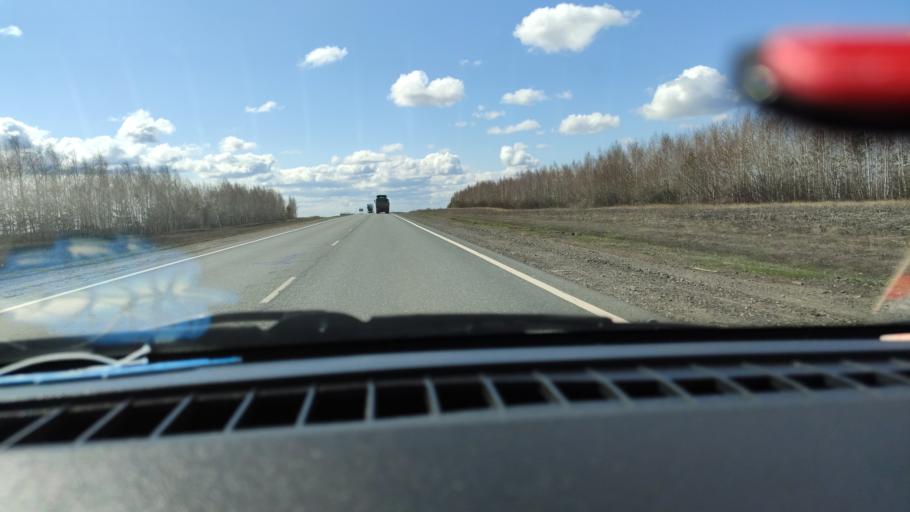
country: RU
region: Saratov
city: Dukhovnitskoye
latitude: 52.8097
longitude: 48.2287
